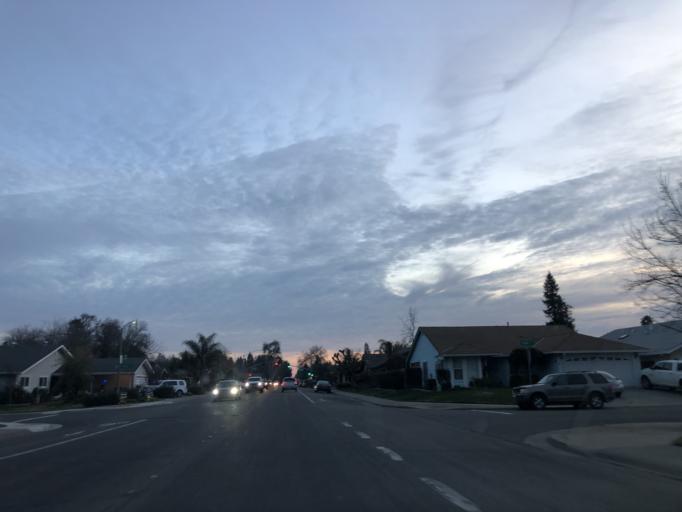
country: US
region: California
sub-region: Yolo County
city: Woodland
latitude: 38.6701
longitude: -121.7563
